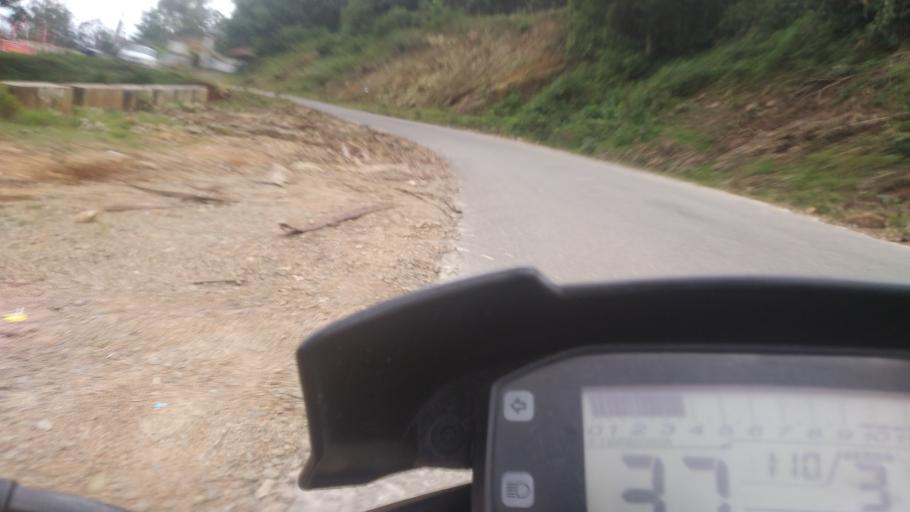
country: IN
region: Kerala
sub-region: Idukki
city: Munnar
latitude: 10.0830
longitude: 77.0705
